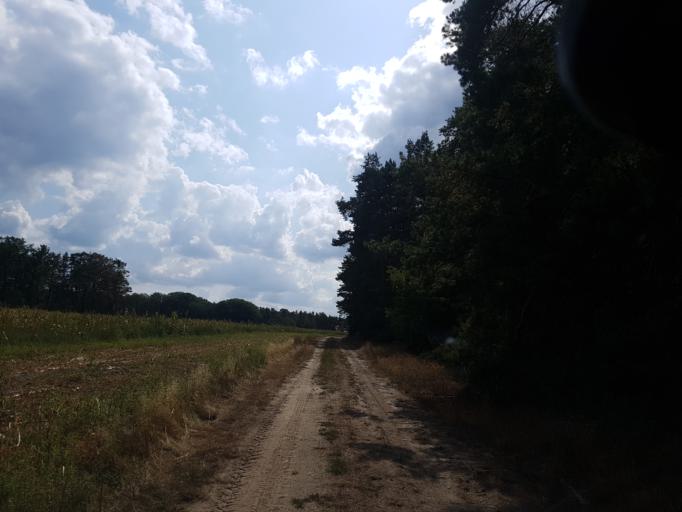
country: DE
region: Brandenburg
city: Calau
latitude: 51.7671
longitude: 13.9660
